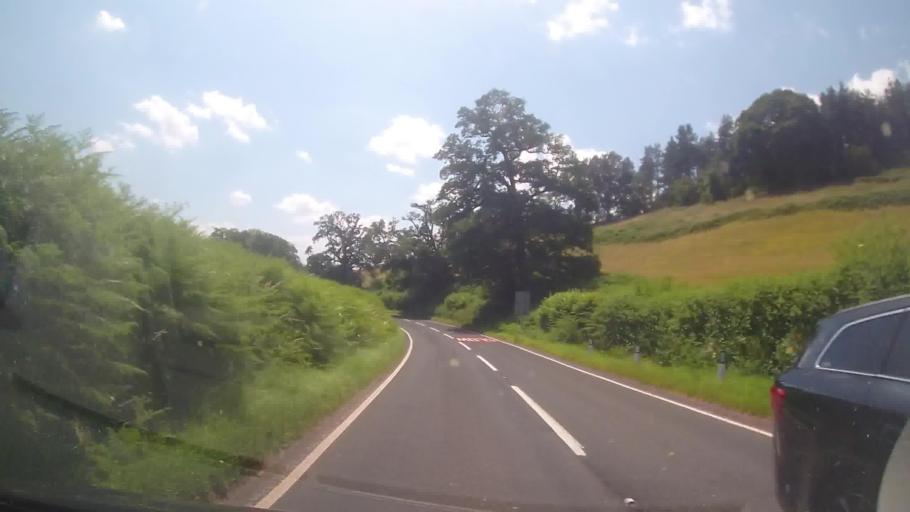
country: GB
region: England
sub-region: Herefordshire
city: Brockhampton
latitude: 51.9914
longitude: -2.5733
